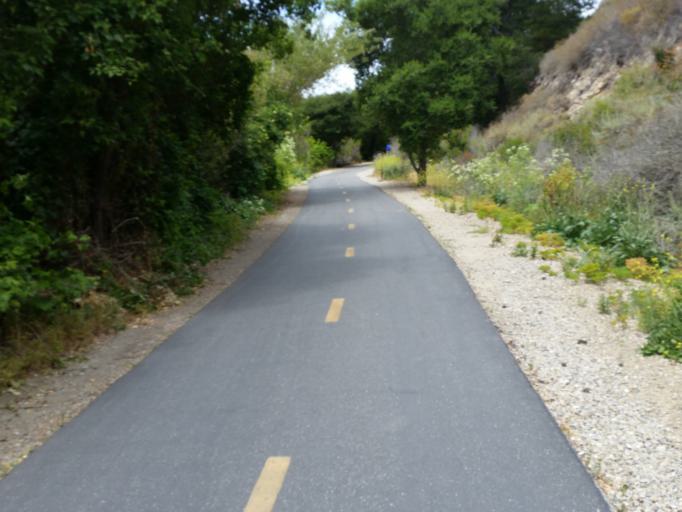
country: US
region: California
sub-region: San Luis Obispo County
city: Avila Beach
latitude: 35.1848
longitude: -120.7058
